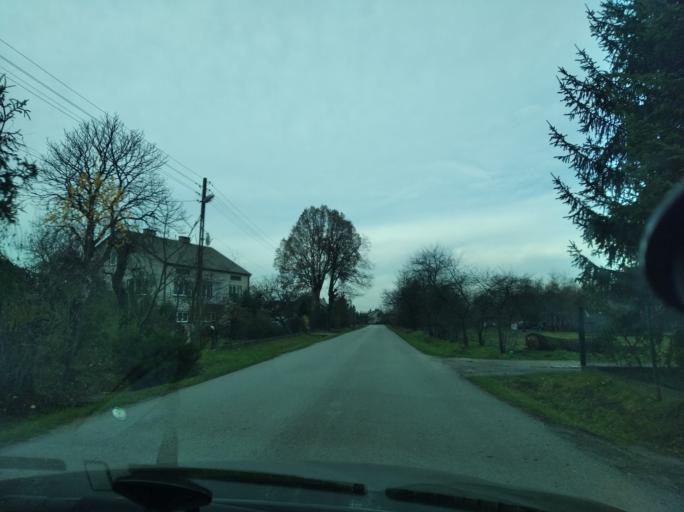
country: PL
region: Subcarpathian Voivodeship
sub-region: Powiat przeworski
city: Grzeska
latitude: 50.0890
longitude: 22.4462
